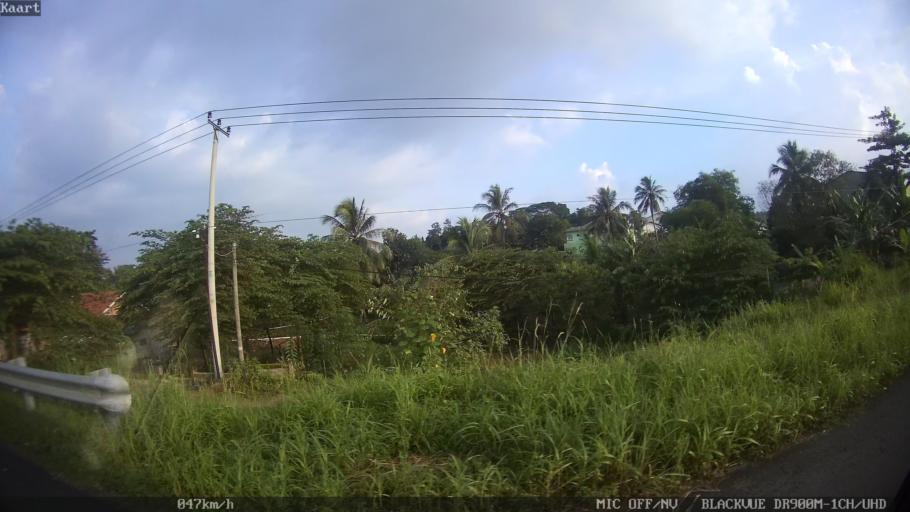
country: ID
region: Lampung
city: Panjang
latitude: -5.4010
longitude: 105.3528
